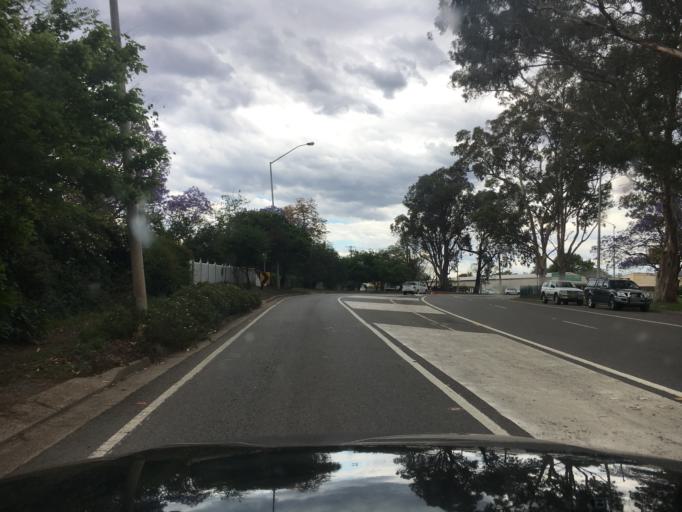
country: AU
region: New South Wales
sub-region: Muswellbrook
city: Muswellbrook
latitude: -32.0456
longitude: 150.8678
